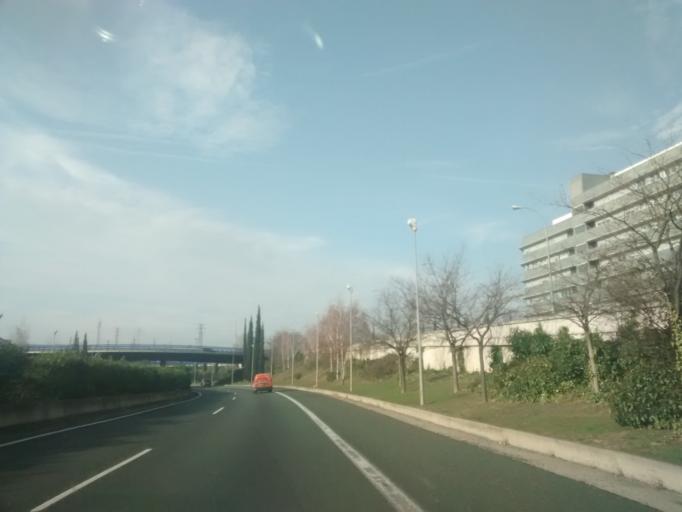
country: ES
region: La Rioja
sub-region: Provincia de La Rioja
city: Logrono
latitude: 42.4564
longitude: -2.4839
